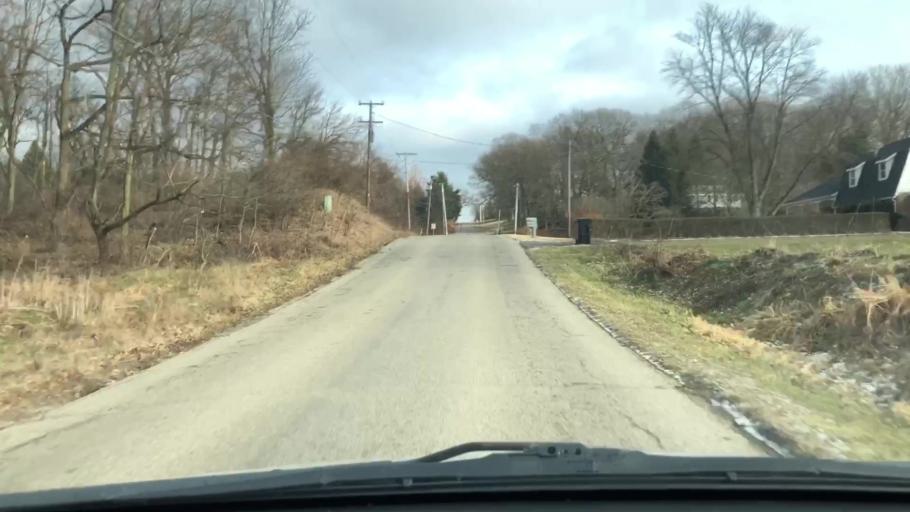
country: US
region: Indiana
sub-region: Steuben County
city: Angola
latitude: 41.6826
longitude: -85.0111
